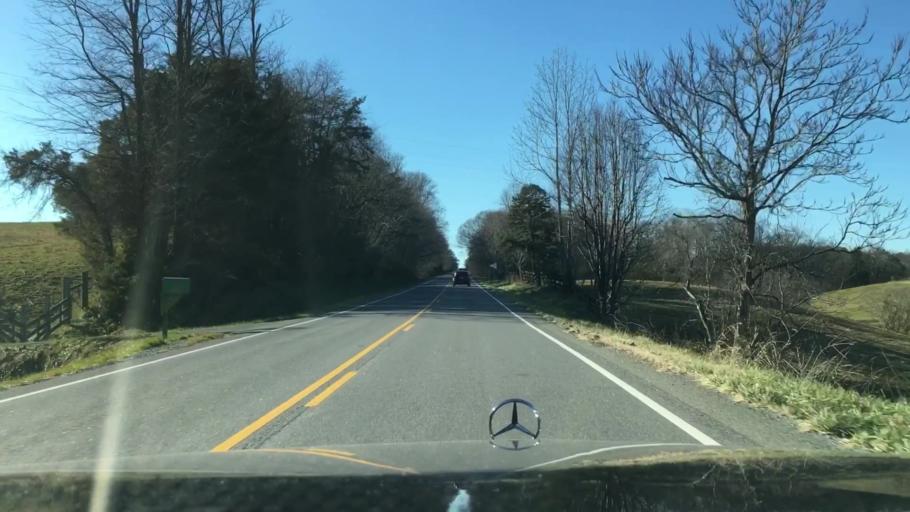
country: US
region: Virginia
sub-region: City of Bedford
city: Bedford
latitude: 37.2410
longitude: -79.6025
